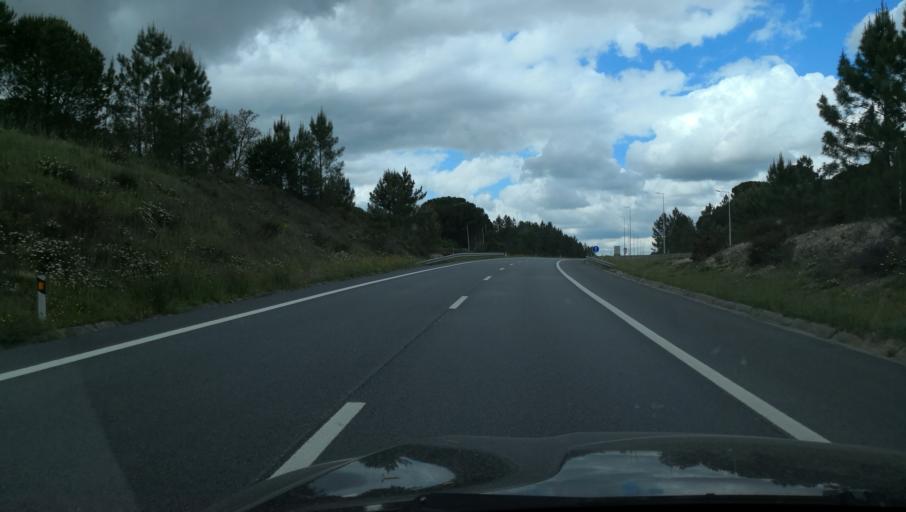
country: PT
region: Evora
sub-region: Vendas Novas
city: Vendas Novas
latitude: 38.6063
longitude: -8.6463
